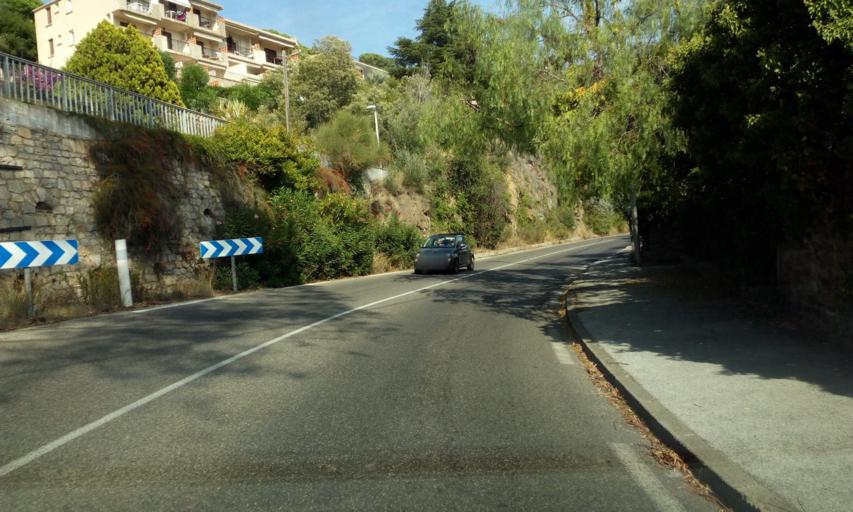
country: FR
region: Provence-Alpes-Cote d'Azur
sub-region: Departement du Var
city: Le Lavandou
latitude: 43.1453
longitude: 6.3865
